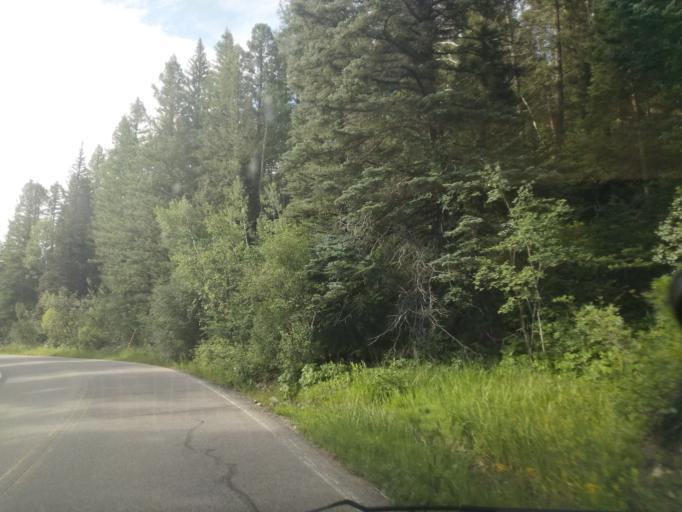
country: US
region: Colorado
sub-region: Garfield County
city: Carbondale
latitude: 39.1079
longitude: -107.2661
